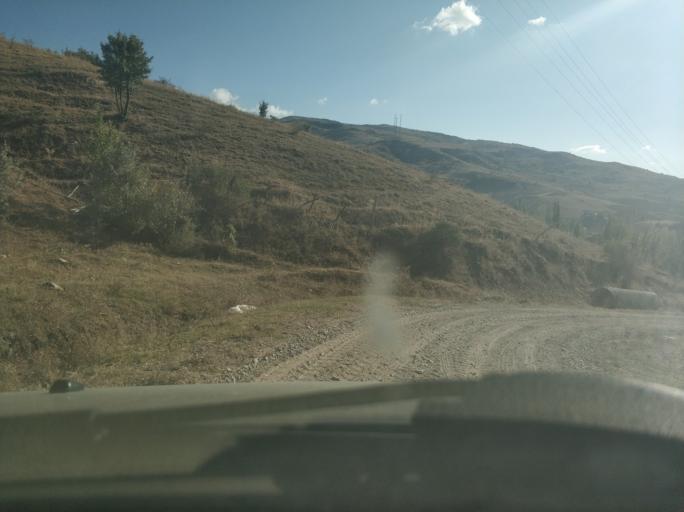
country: TR
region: Sivas
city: Zara
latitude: 39.8280
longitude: 37.8967
